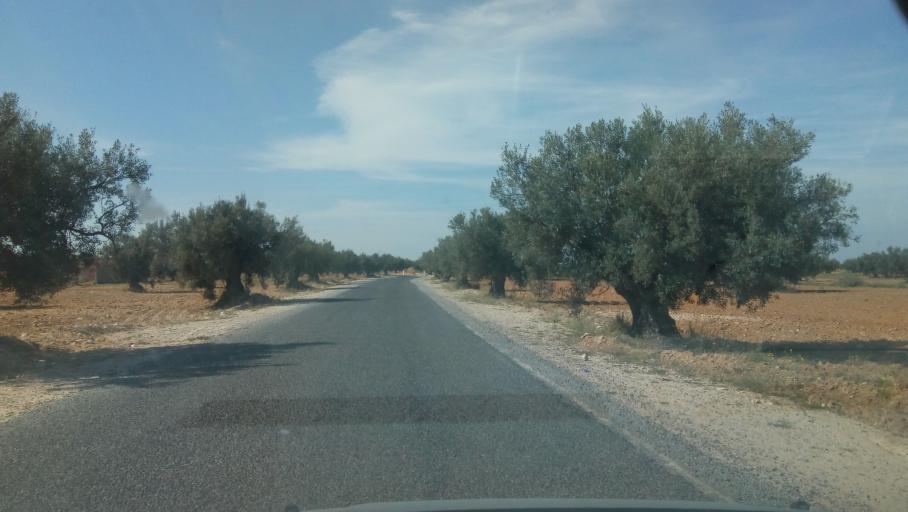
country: TN
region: Safaqis
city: Al Qarmadah
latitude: 34.8764
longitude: 10.8805
